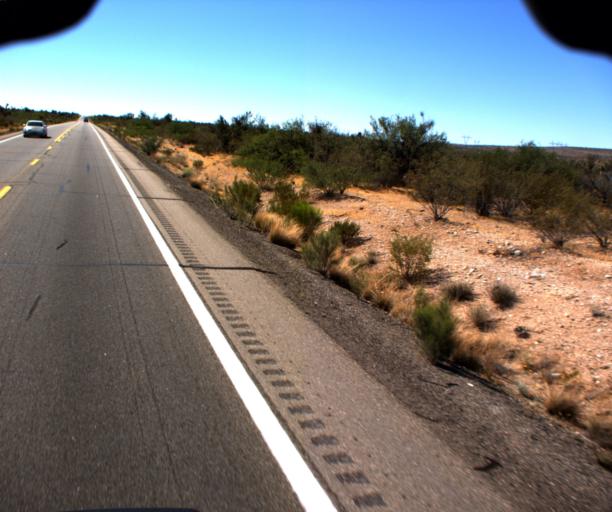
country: US
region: Arizona
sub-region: Yavapai County
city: Bagdad
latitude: 34.3013
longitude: -113.1193
